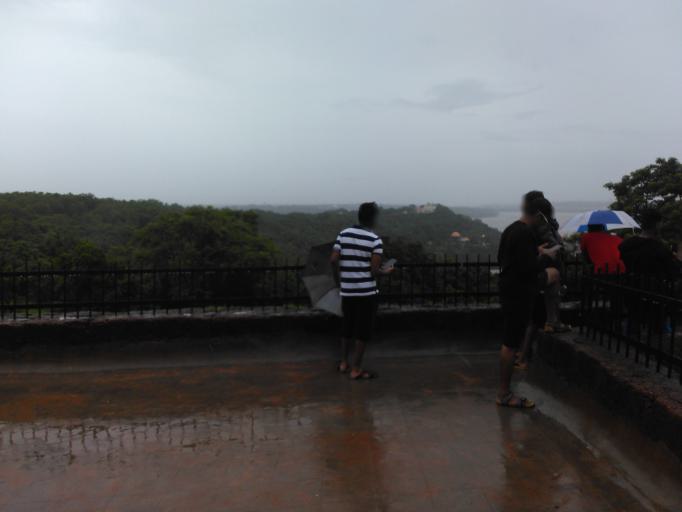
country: IN
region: Goa
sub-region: North Goa
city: Candolim
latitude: 15.4921
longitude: 73.7742
